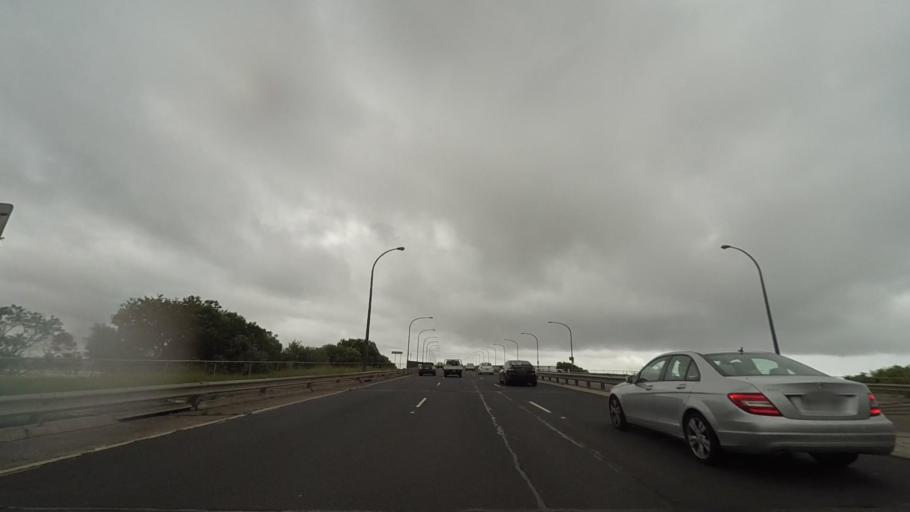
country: AU
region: New South Wales
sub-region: Rockdale
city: Dolls Point
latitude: -34.0110
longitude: 151.1263
